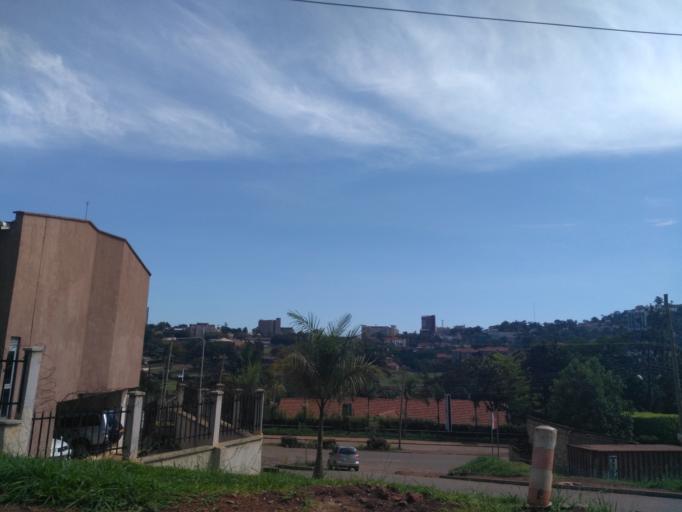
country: UG
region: Central Region
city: Kampala Central Division
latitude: 0.3311
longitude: 32.5799
